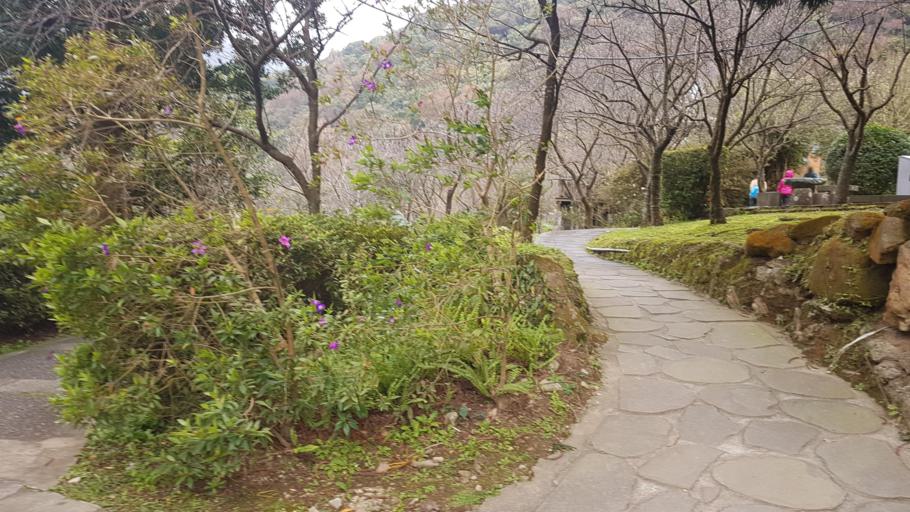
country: TW
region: Taipei
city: Taipei
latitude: 25.1581
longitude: 121.5397
